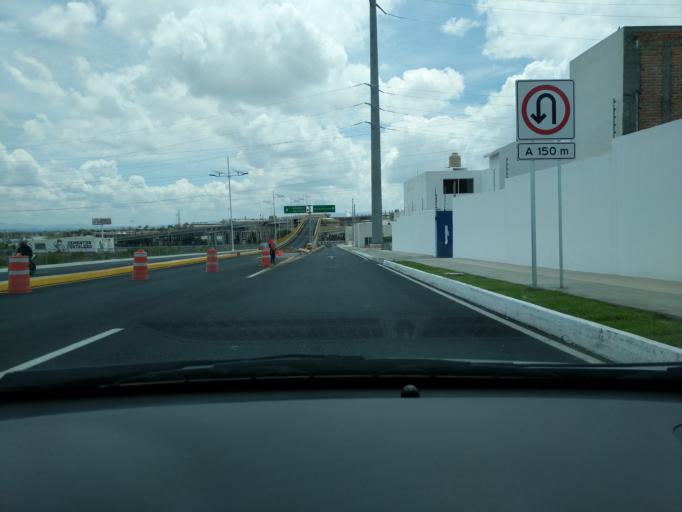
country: MX
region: San Luis Potosi
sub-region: Mexquitic de Carmona
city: Guadalupe Victoria
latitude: 22.1689
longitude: -101.0428
